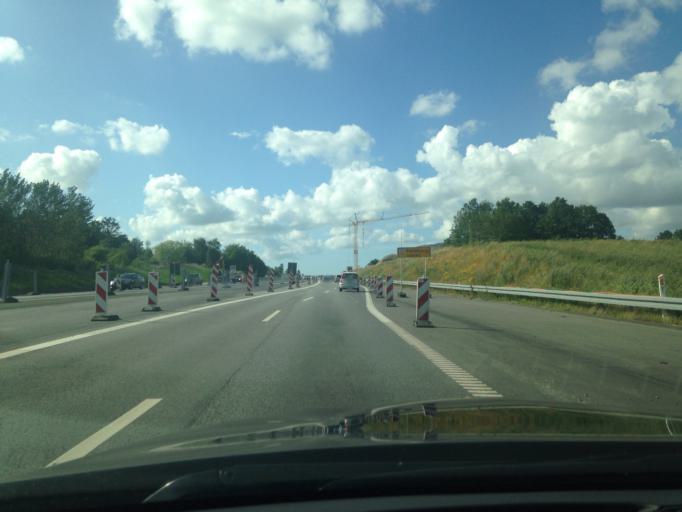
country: DK
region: Capital Region
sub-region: Rudersdal Kommune
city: Trorod
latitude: 55.8448
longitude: 12.5089
